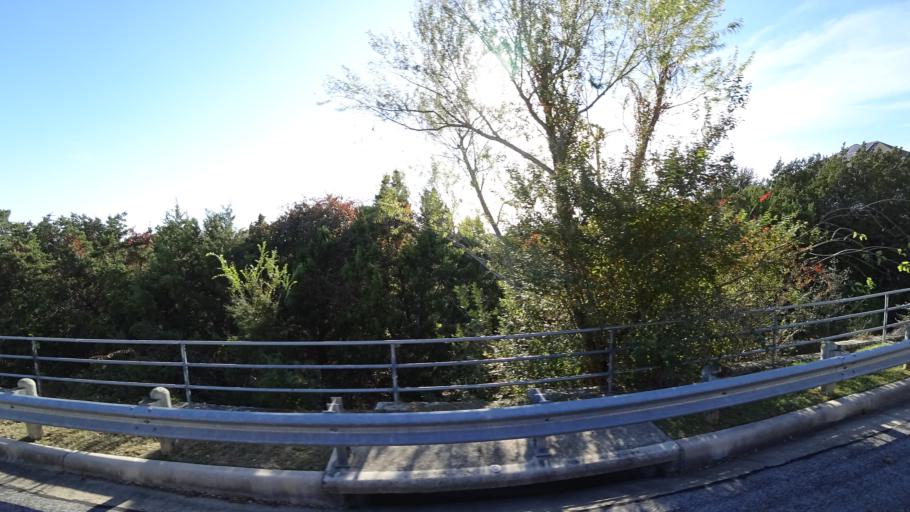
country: US
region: Texas
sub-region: Williamson County
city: Jollyville
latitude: 30.4094
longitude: -97.7749
